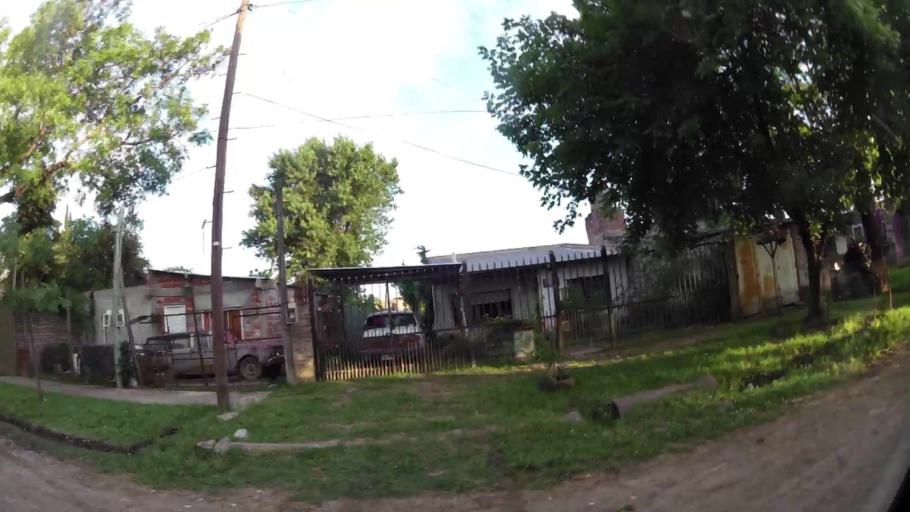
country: AR
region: Buenos Aires
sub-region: Partido de Merlo
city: Merlo
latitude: -34.6708
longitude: -58.7728
